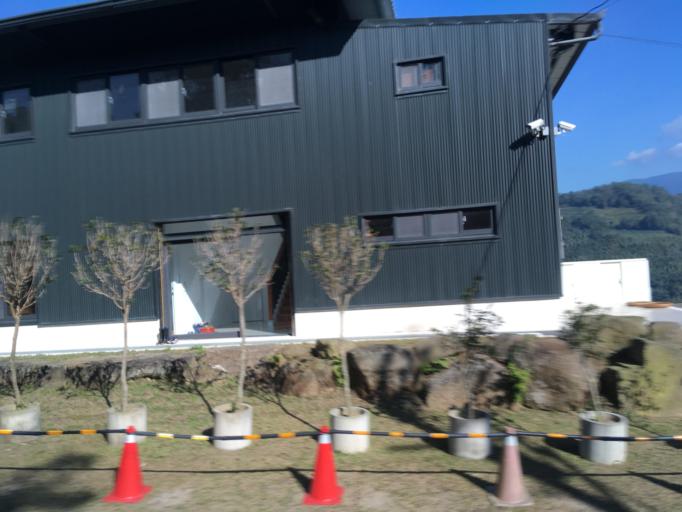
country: TW
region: Taiwan
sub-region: Chiayi
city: Jiayi Shi
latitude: 23.4065
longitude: 120.6544
